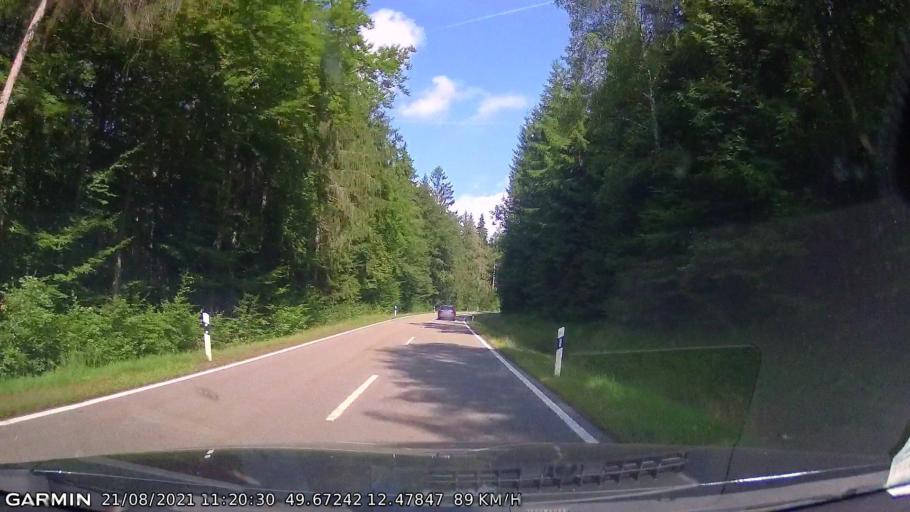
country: DE
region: Bavaria
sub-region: Upper Palatinate
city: Waidhaus
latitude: 49.6724
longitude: 12.4784
